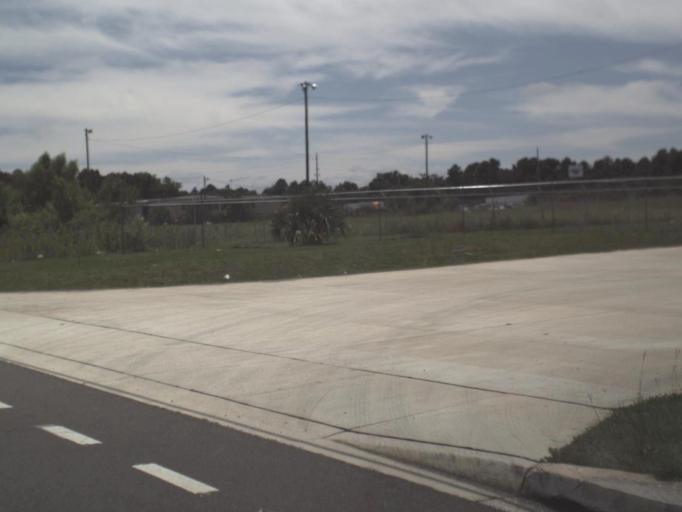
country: US
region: Florida
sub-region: Duval County
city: Jacksonville
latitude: 30.3678
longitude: -81.7226
